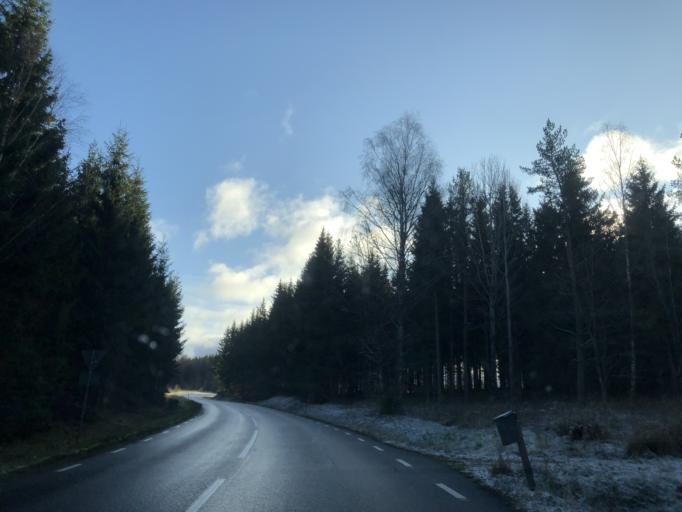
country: SE
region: Vaestra Goetaland
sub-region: Tranemo Kommun
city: Limmared
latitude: 57.6305
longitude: 13.4496
